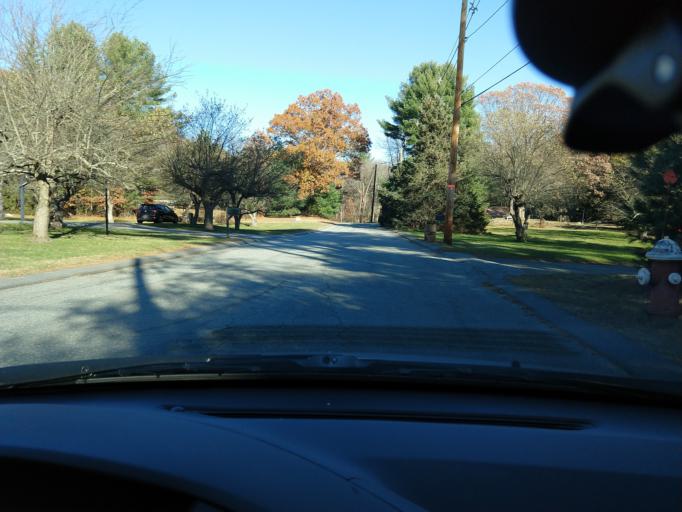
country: US
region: Massachusetts
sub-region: Middlesex County
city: Bedford
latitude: 42.5193
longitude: -71.2883
